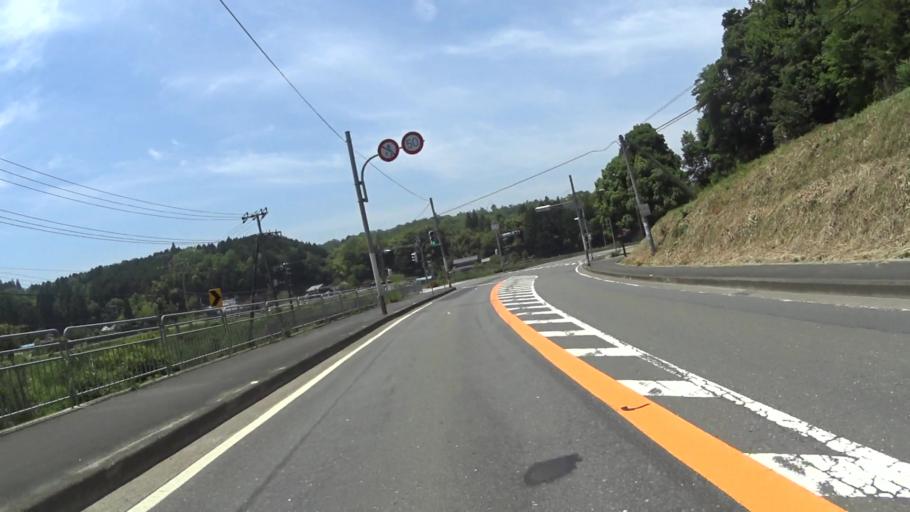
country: JP
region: Kyoto
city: Ayabe
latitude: 35.1794
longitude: 135.3492
